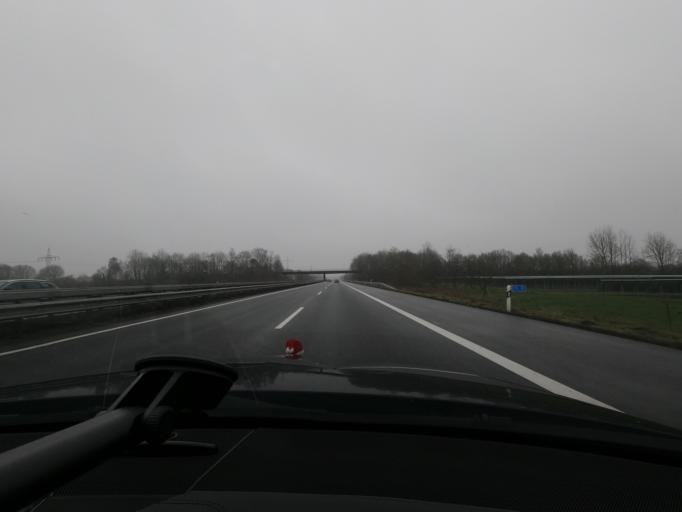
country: DE
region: Schleswig-Holstein
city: Bokel
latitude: 54.2512
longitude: 9.8092
